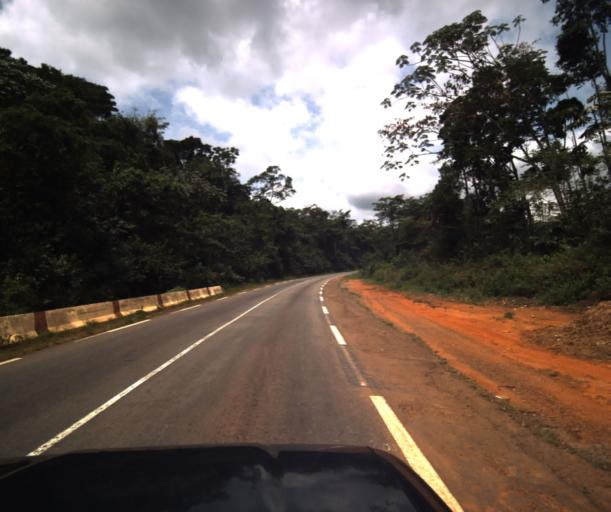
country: CM
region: Centre
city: Mbankomo
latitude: 3.7712
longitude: 11.1702
